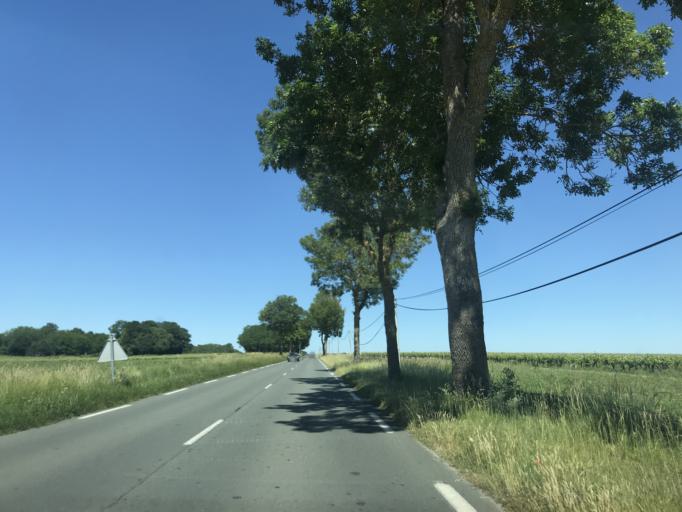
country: FR
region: Poitou-Charentes
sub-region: Departement de la Charente-Maritime
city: Gemozac
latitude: 45.5680
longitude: -0.7351
